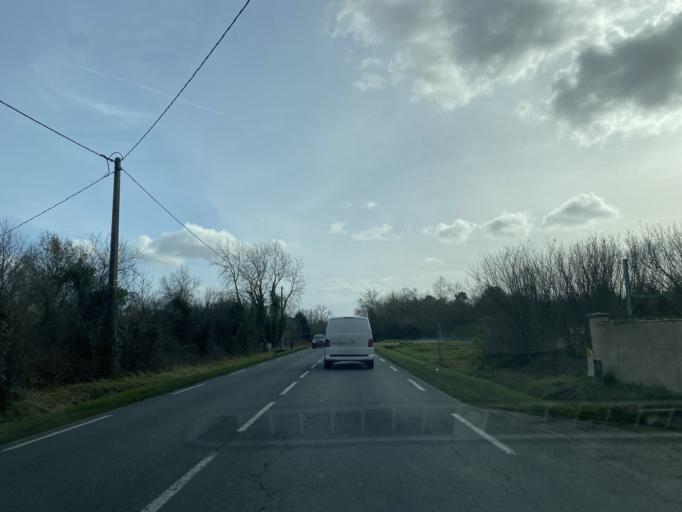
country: FR
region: Aquitaine
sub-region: Departement de la Gironde
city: Le Taillan-Medoc
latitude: 44.9263
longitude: -0.6775
